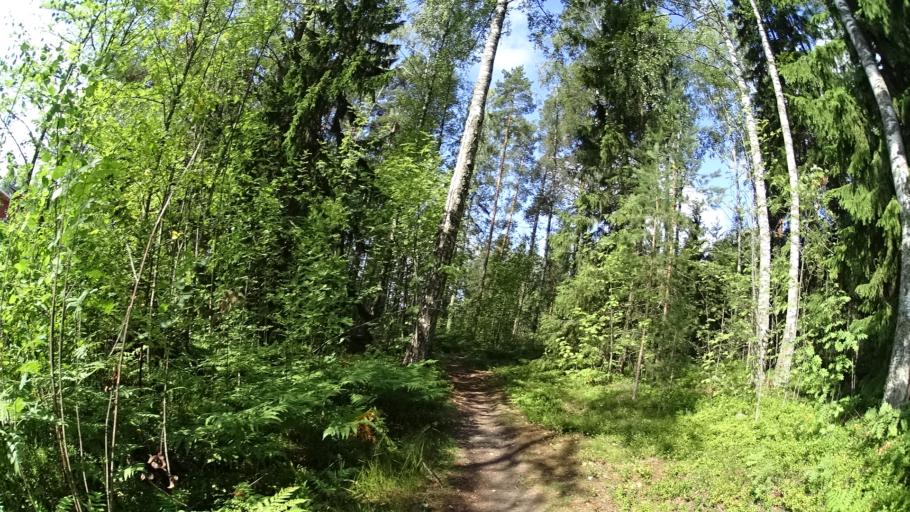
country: FI
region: Uusimaa
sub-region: Helsinki
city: Teekkarikylae
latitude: 60.2879
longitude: 24.8994
